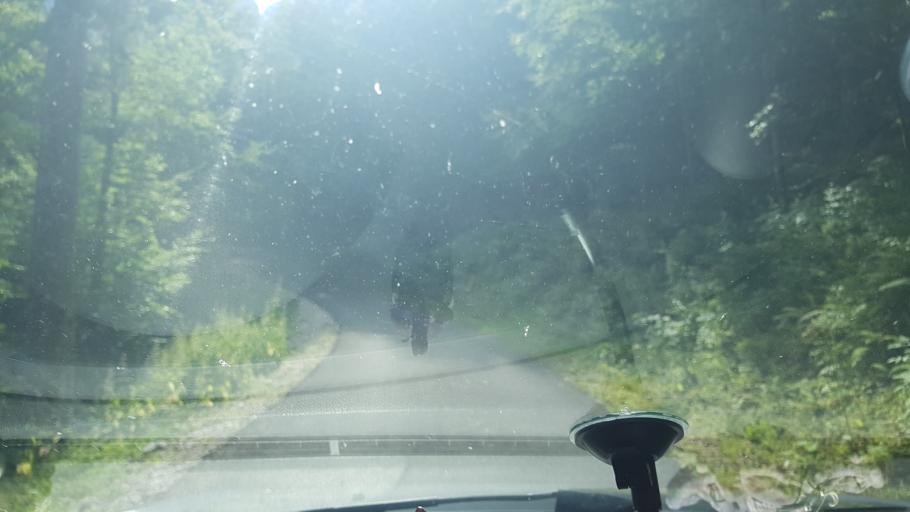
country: IT
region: Friuli Venezia Giulia
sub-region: Provincia di Udine
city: Taipana
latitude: 46.3316
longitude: 13.4189
